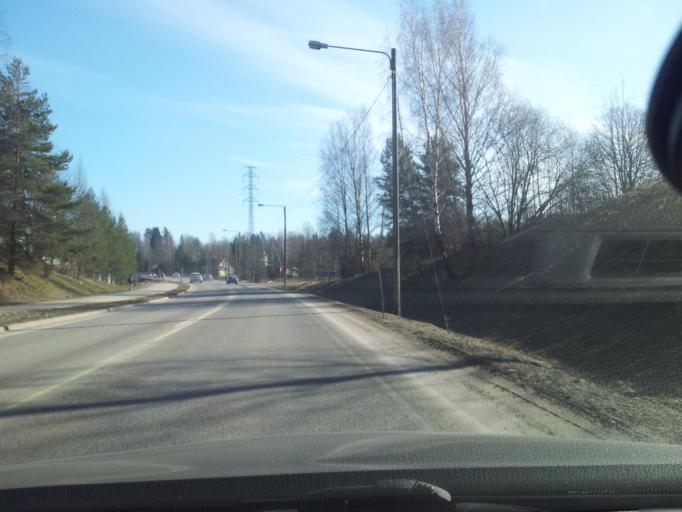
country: FI
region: Uusimaa
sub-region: Helsinki
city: Espoo
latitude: 60.1858
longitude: 24.5894
